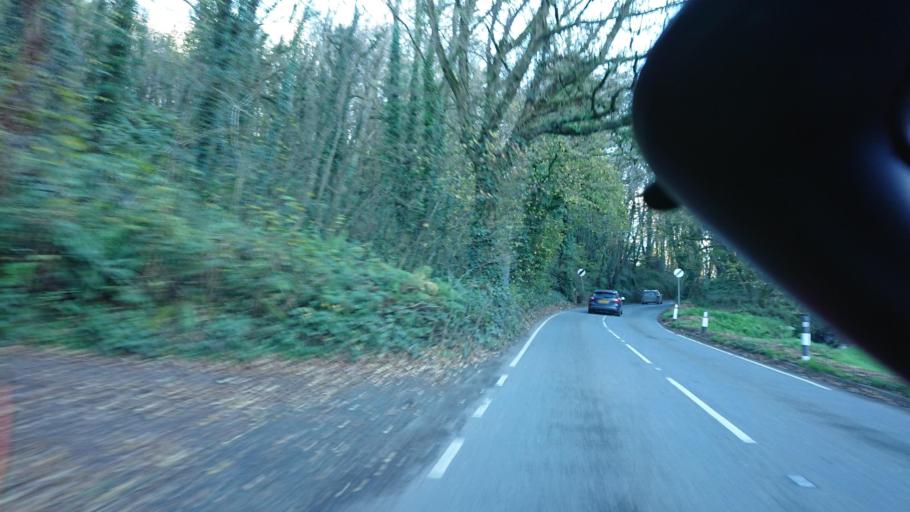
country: GB
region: England
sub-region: Cornwall
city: Looe
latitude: 50.3920
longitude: -4.3846
